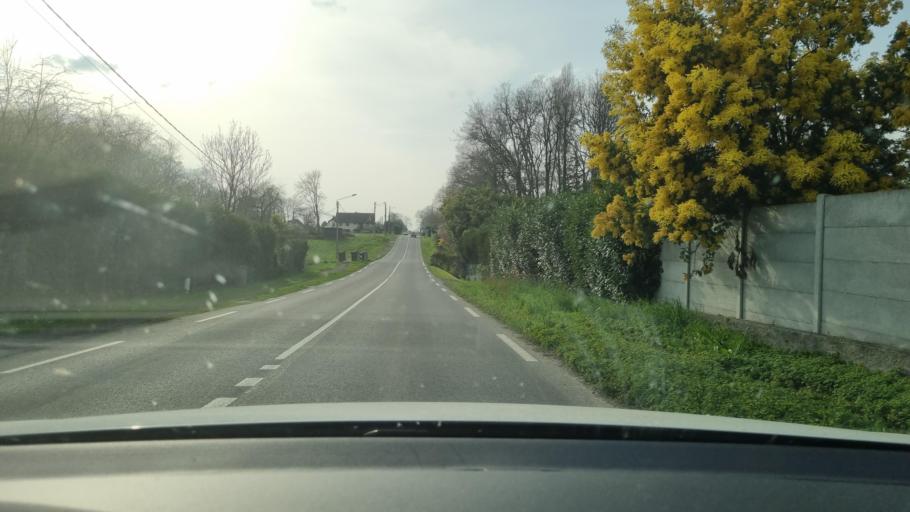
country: FR
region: Aquitaine
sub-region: Departement des Pyrenees-Atlantiques
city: Morlaas
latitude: 43.3586
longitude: -0.2339
